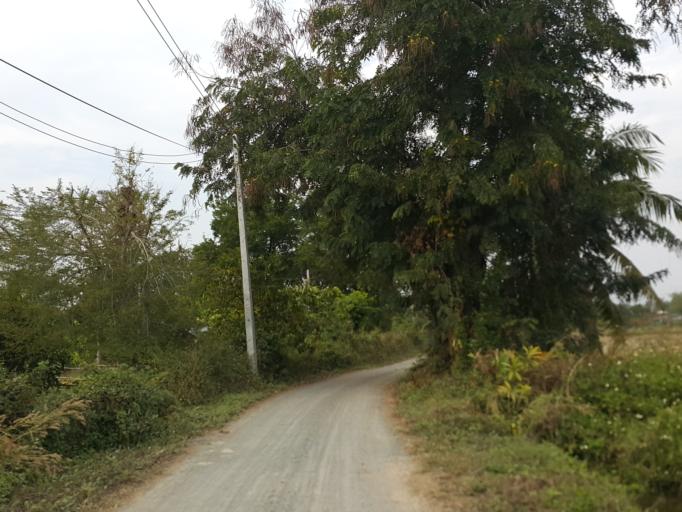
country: TH
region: Chiang Mai
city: San Kamphaeng
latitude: 18.8334
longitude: 99.1519
